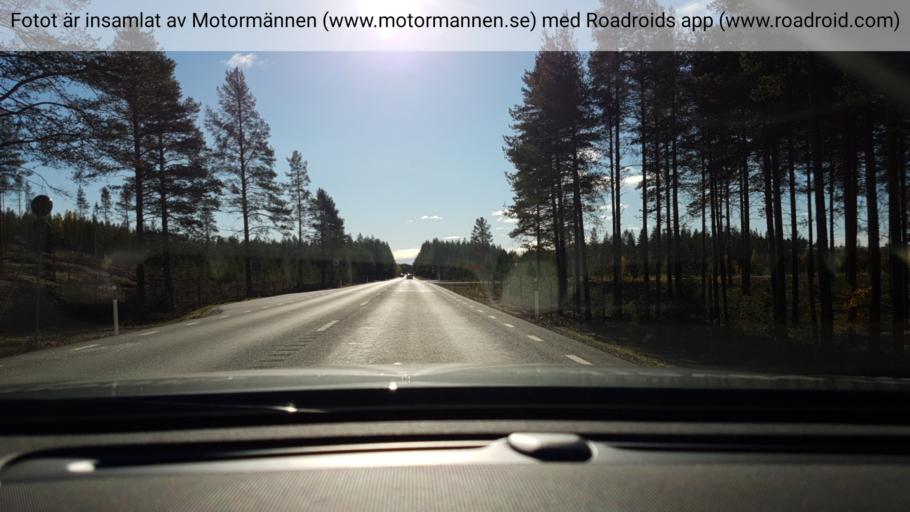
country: SE
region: Vaesterbotten
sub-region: Skelleftea Kommun
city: Burea
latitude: 64.5643
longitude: 21.2312
